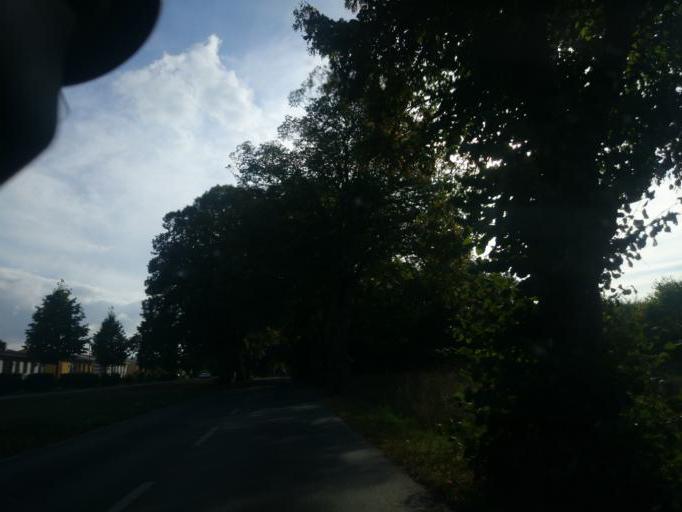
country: DE
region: Mecklenburg-Vorpommern
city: Bad Doberan
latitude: 54.1132
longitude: 11.9109
